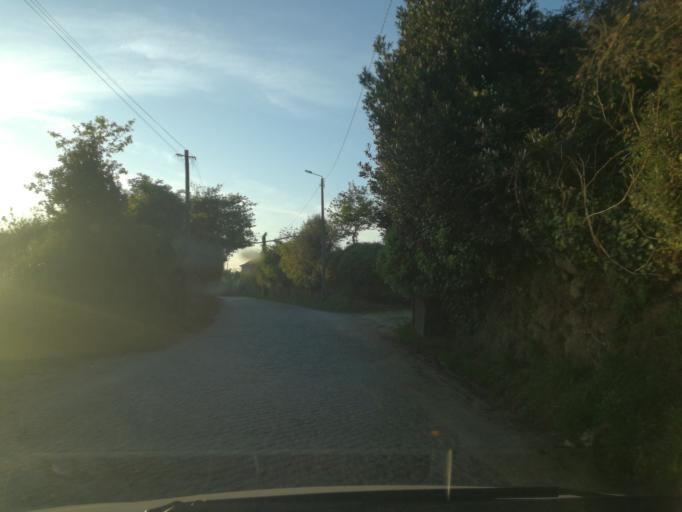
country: PT
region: Porto
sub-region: Matosinhos
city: Santa Cruz do Bispo
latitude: 41.2602
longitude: -8.6805
